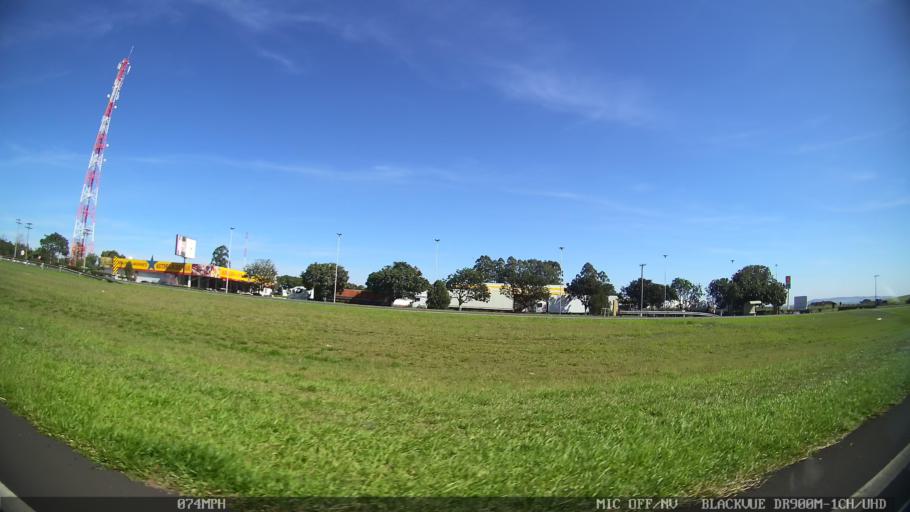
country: BR
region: Sao Paulo
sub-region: Santa Rita Do Passa Quatro
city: Santa Rita do Passa Quatro
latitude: -21.6788
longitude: -47.6040
